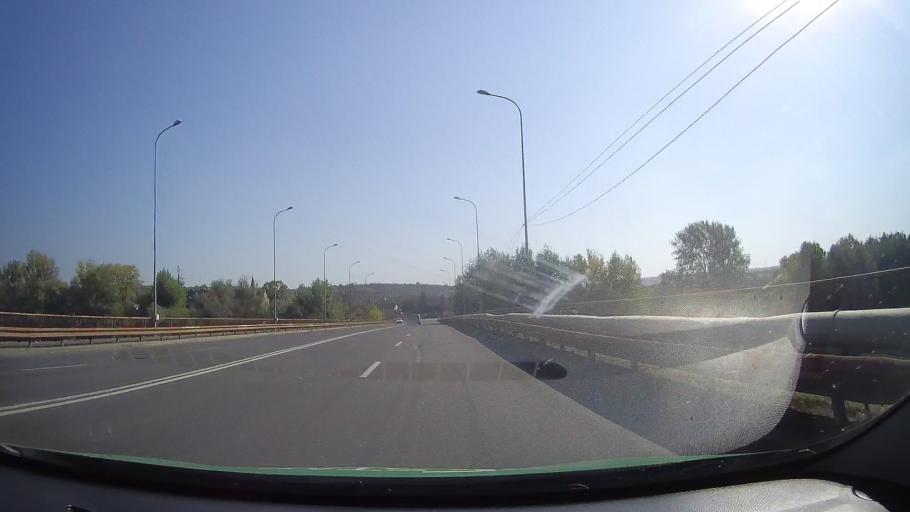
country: RO
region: Arad
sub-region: Oras Lipova
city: Radna
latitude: 46.0904
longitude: 21.6891
